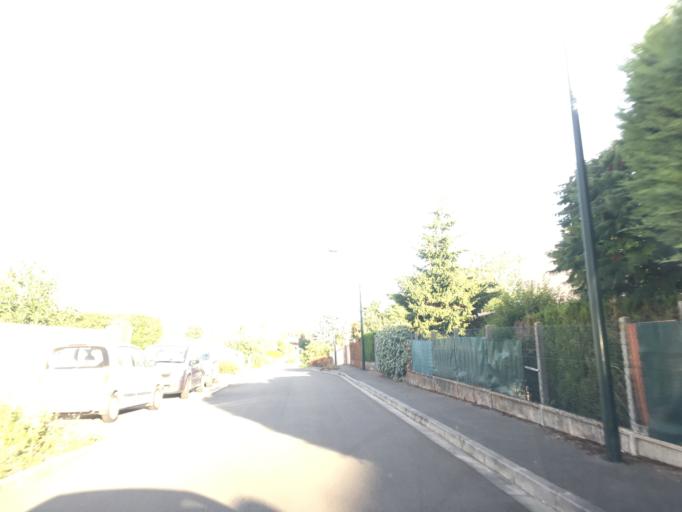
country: FR
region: Haute-Normandie
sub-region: Departement de l'Eure
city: Vernon
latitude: 49.0832
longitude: 1.4950
